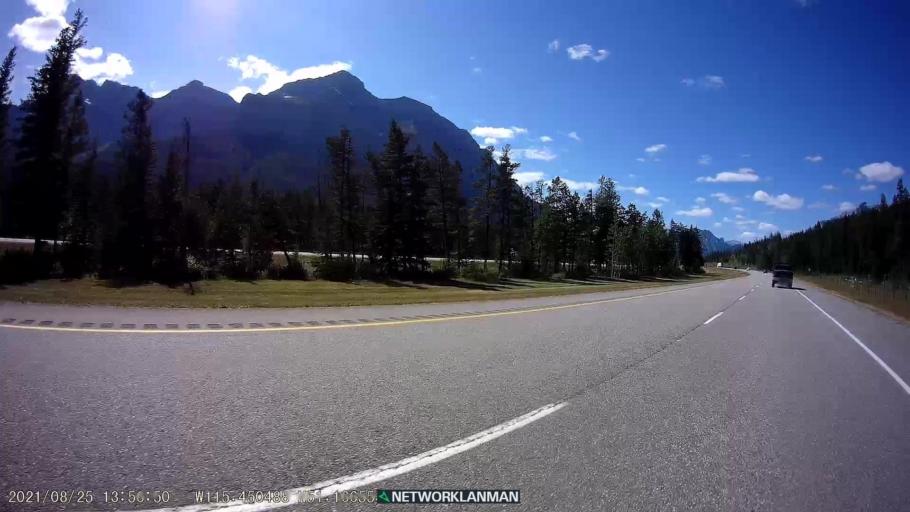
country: CA
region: Alberta
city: Banff
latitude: 51.1670
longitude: -115.4506
